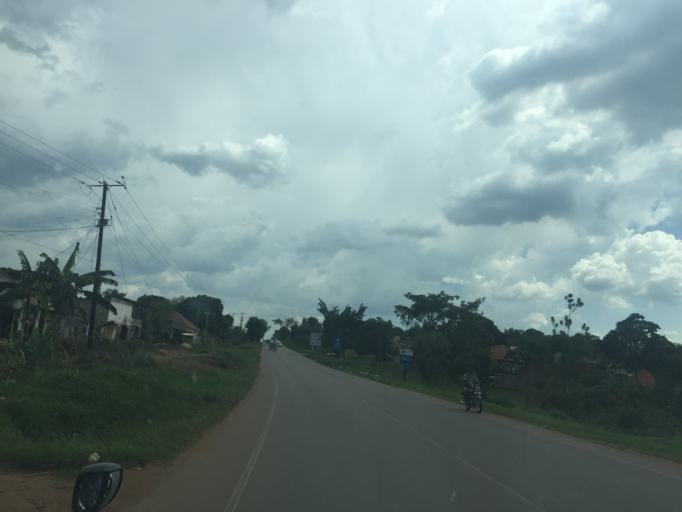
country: UG
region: Central Region
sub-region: Luwero District
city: Wobulenzi
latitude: 0.6985
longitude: 32.5226
